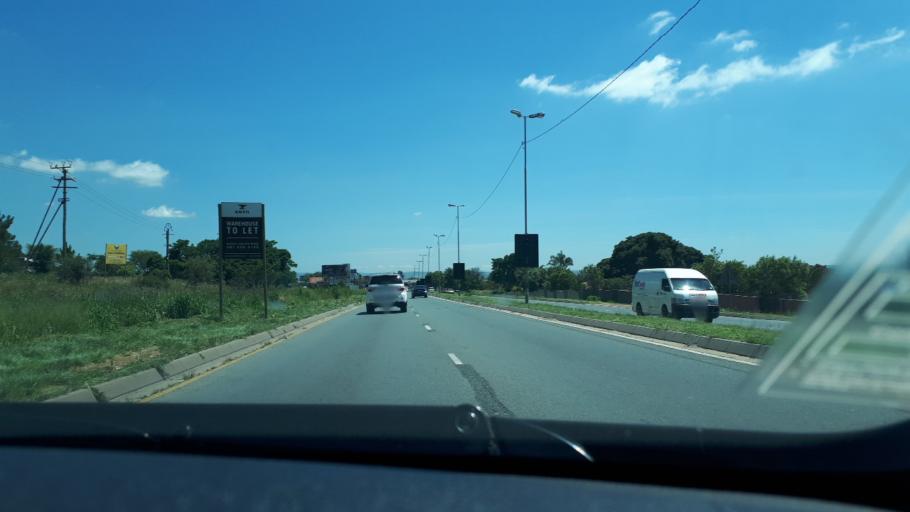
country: ZA
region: Gauteng
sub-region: West Rand District Municipality
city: Muldersdriseloop
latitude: -26.0525
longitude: 27.9558
